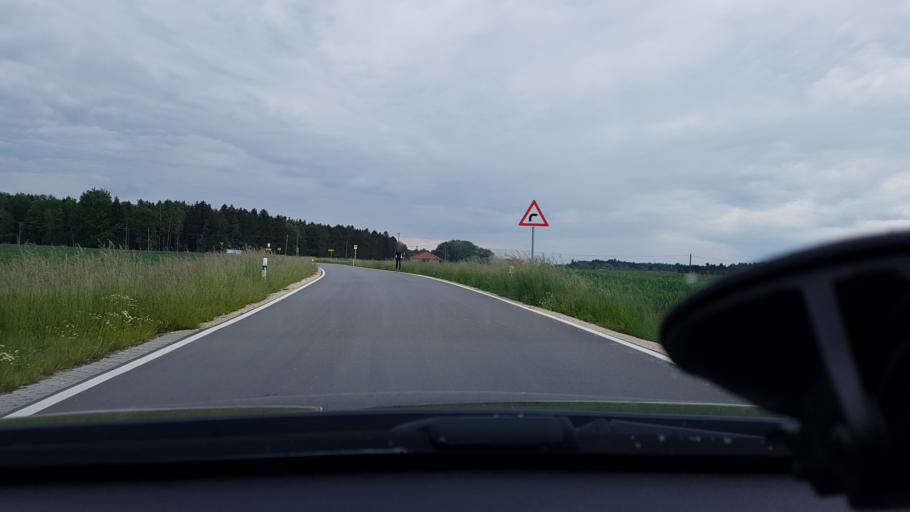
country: DE
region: Bavaria
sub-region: Lower Bavaria
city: Stubenberg
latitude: 48.3310
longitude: 13.0578
